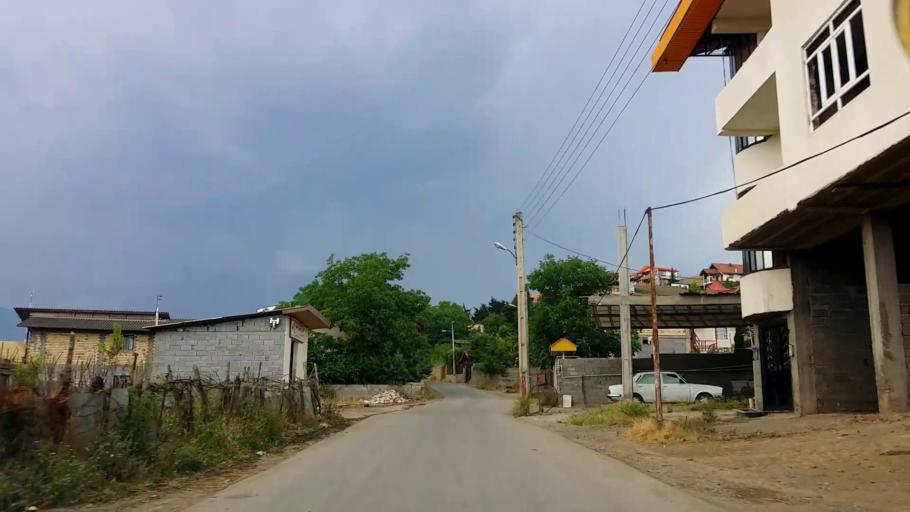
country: IR
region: Mazandaran
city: Chalus
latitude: 36.5153
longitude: 51.2522
